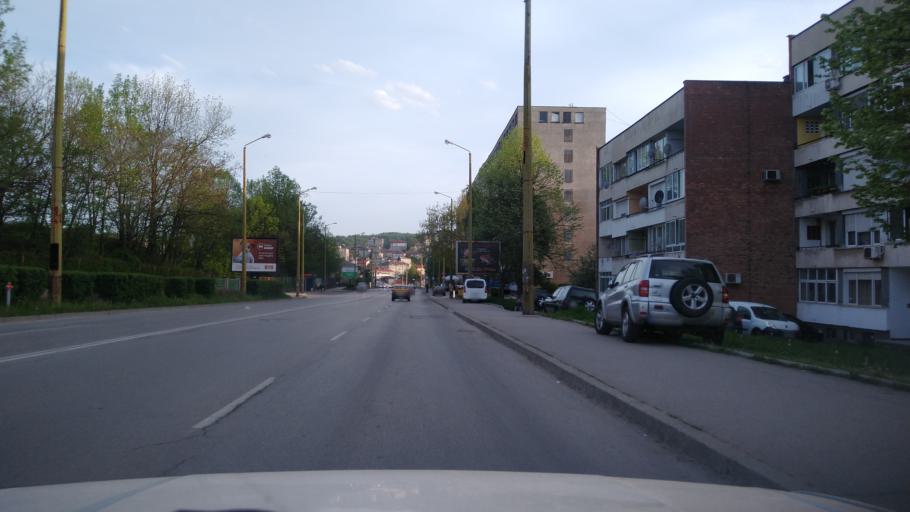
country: BG
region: Gabrovo
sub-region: Obshtina Gabrovo
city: Gabrovo
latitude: 42.8843
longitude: 25.3130
